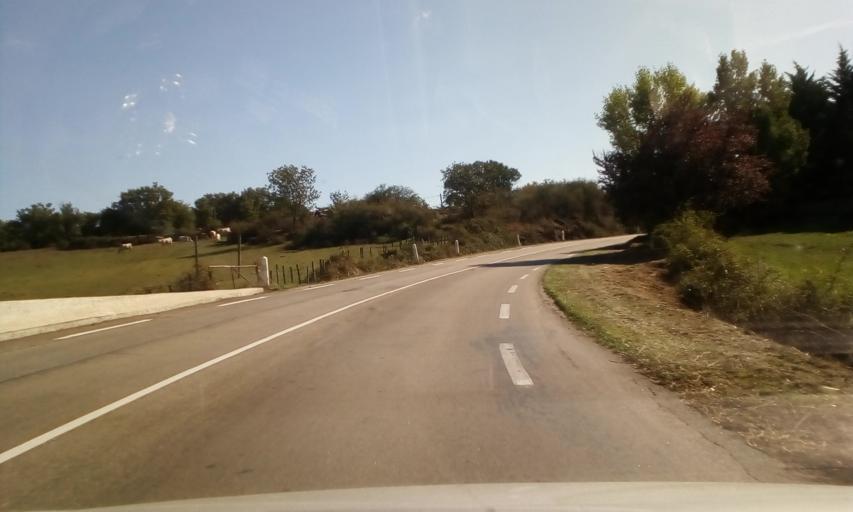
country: FR
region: Rhone-Alpes
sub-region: Departement de l'Ardeche
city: Annonay
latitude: 45.2499
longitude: 4.6795
